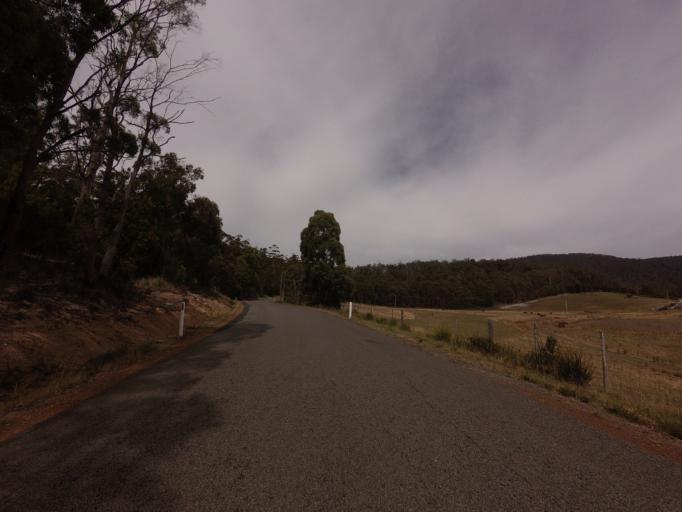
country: AU
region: Tasmania
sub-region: Sorell
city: Sorell
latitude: -42.5794
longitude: 147.5595
